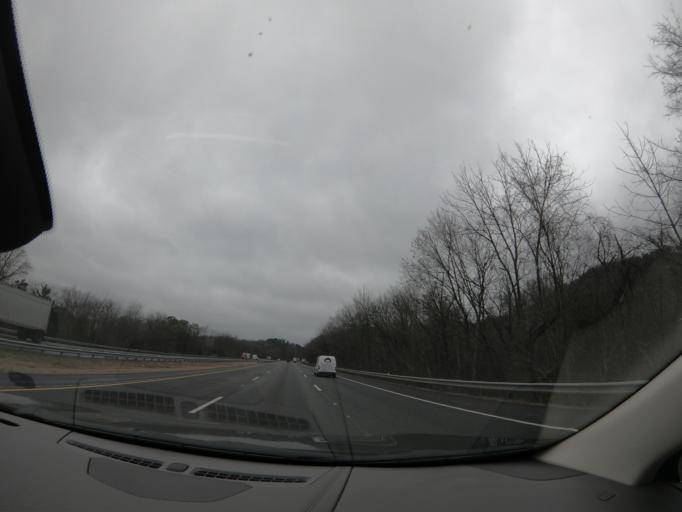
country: US
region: Georgia
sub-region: Whitfield County
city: Dalton
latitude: 34.8030
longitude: -85.0114
